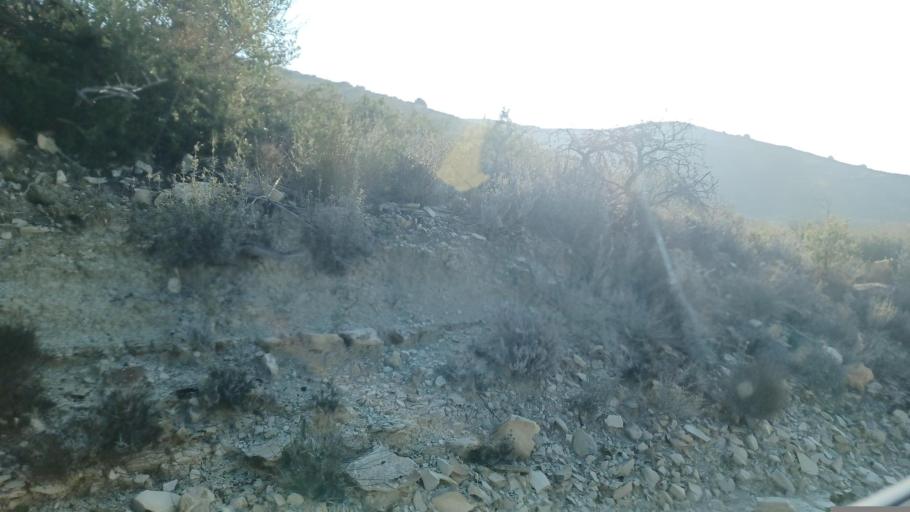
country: CY
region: Larnaka
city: Kofinou
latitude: 34.8325
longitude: 33.3050
